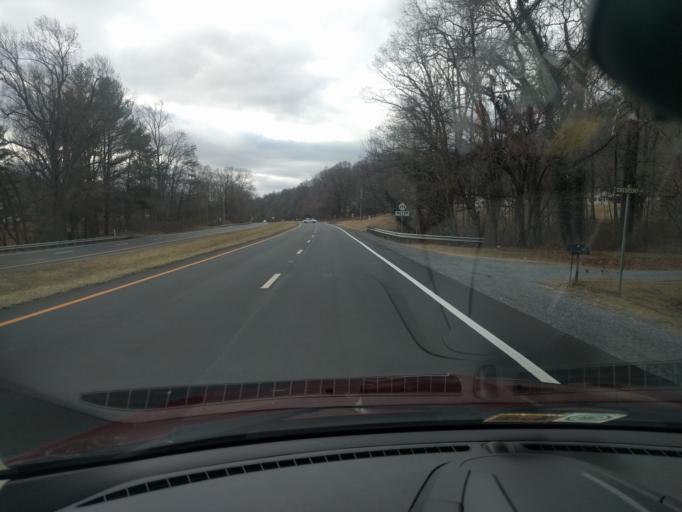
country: US
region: Virginia
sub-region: Botetourt County
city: Blue Ridge
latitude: 37.3959
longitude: -79.7742
